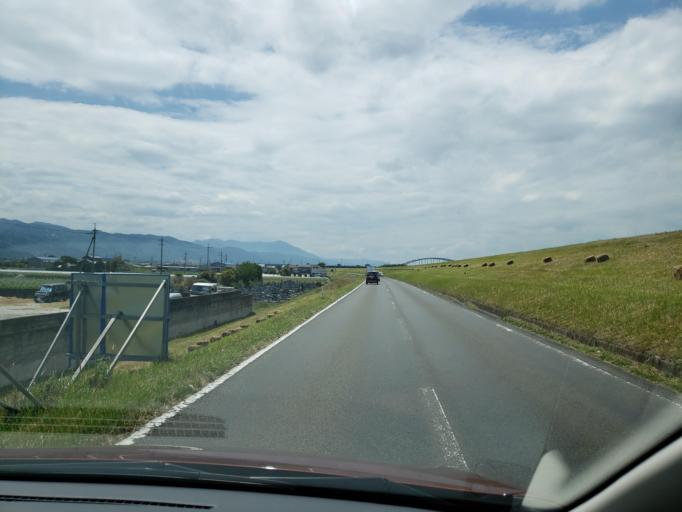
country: JP
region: Tokushima
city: Kamojimacho-jogejima
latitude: 34.0893
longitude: 134.3962
